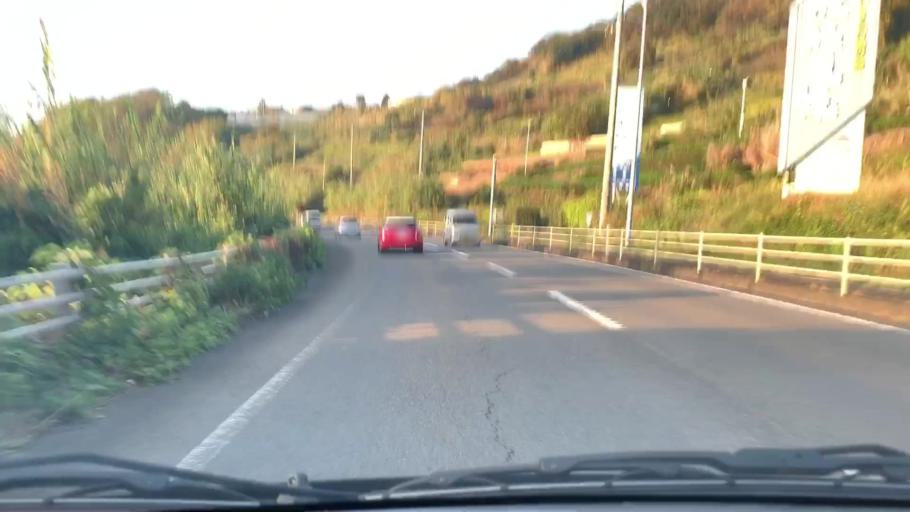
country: JP
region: Nagasaki
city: Omura
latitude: 32.9955
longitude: 129.9488
